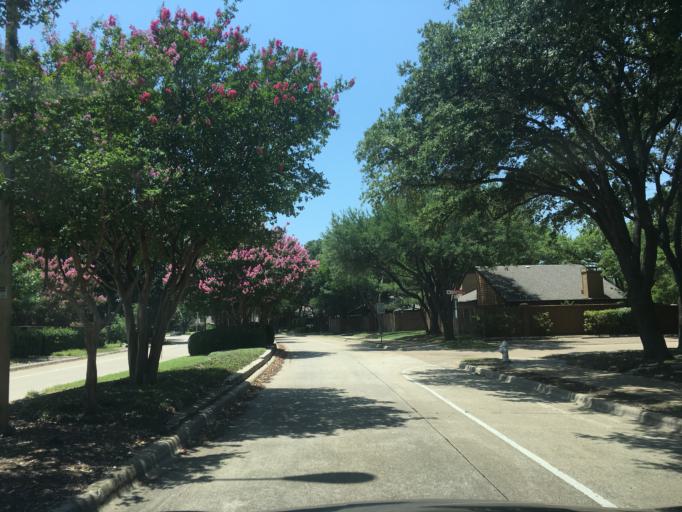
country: US
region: Texas
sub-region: Dallas County
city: Carrollton
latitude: 32.9490
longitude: -96.8649
